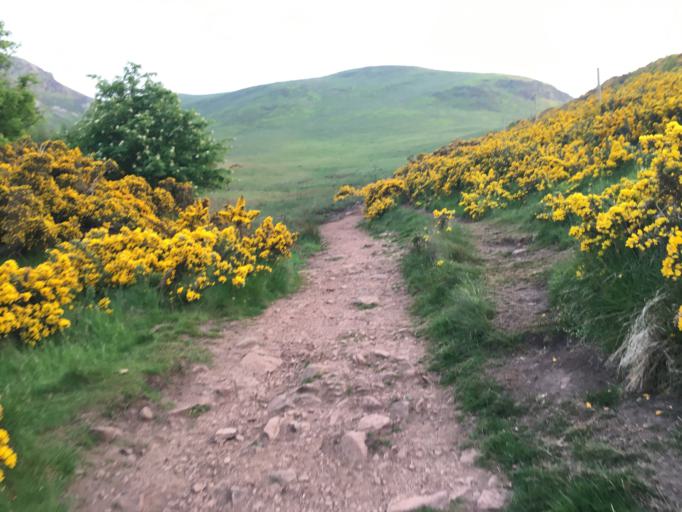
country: GB
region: Scotland
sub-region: Edinburgh
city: Colinton
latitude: 55.8874
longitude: -3.2214
